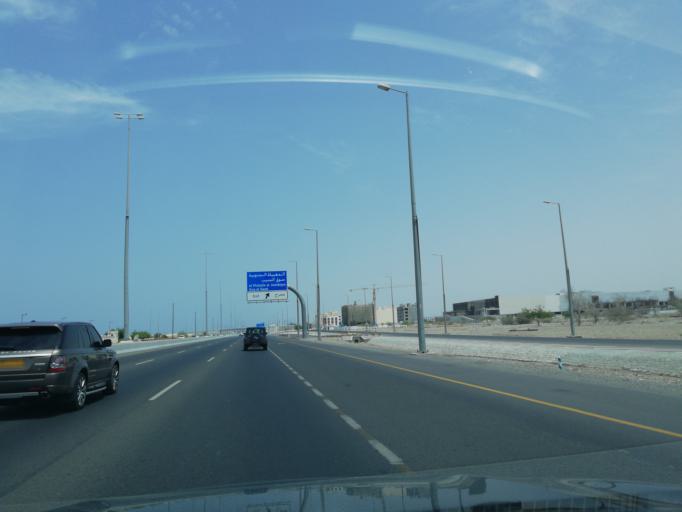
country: OM
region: Muhafazat Masqat
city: As Sib al Jadidah
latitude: 23.6609
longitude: 58.1788
